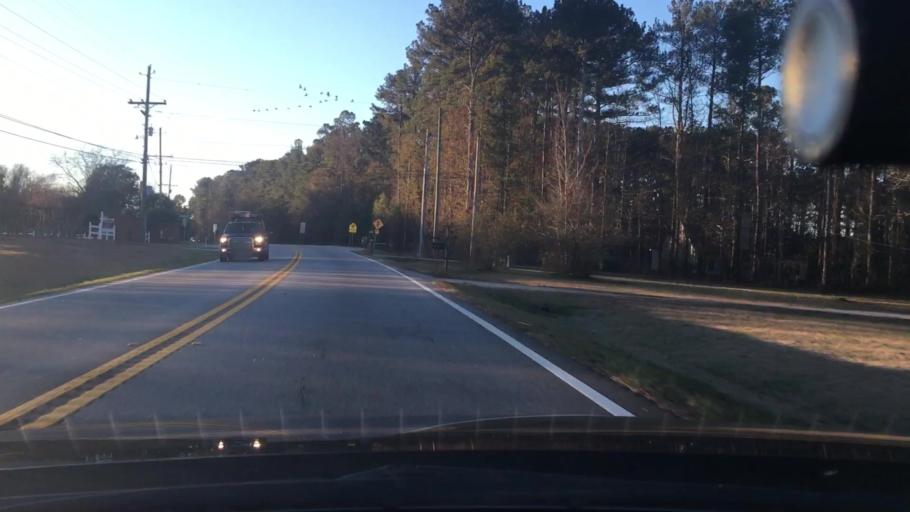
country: US
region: Georgia
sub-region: Fayette County
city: Peachtree City
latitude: 33.4036
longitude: -84.6821
